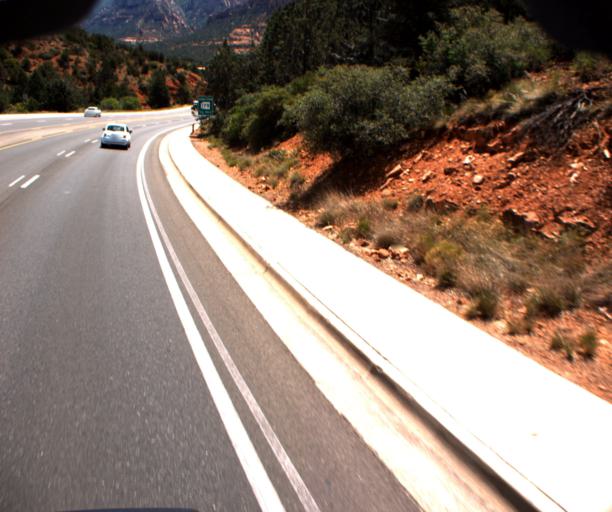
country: US
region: Arizona
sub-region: Coconino County
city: Sedona
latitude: 34.8674
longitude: -111.7707
